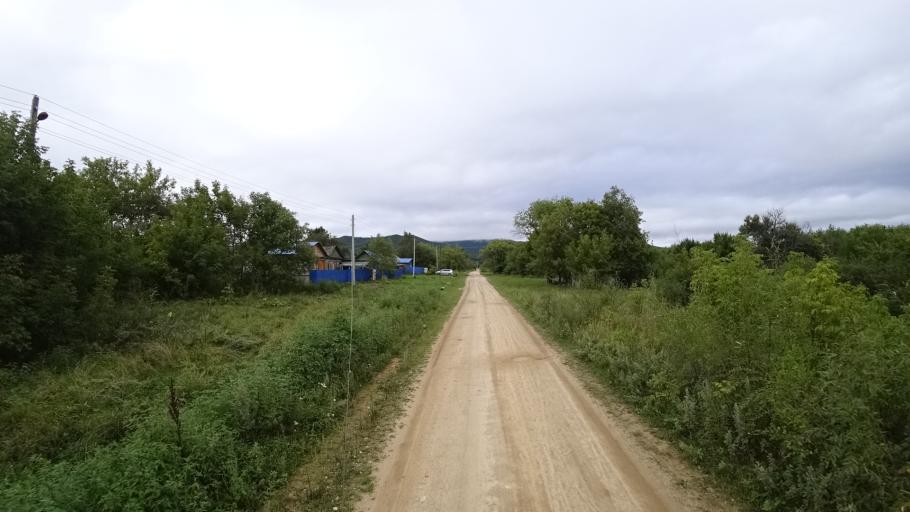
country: RU
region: Primorskiy
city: Rettikhovka
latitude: 44.1349
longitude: 132.6438
